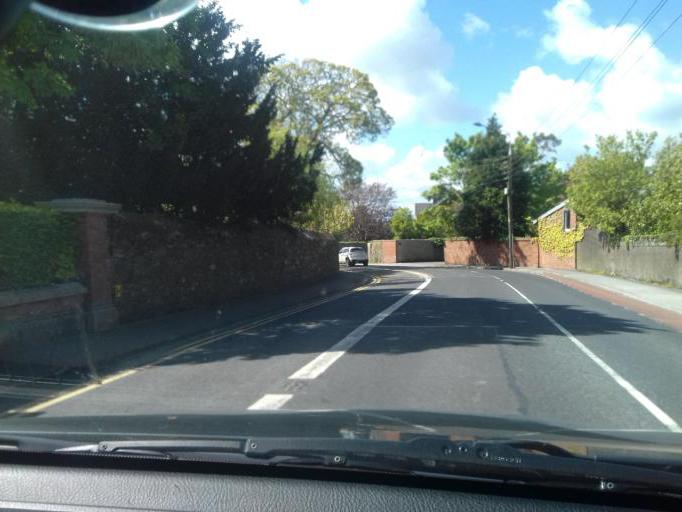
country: IE
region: Munster
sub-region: Waterford
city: Waterford
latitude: 52.2516
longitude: -7.0966
